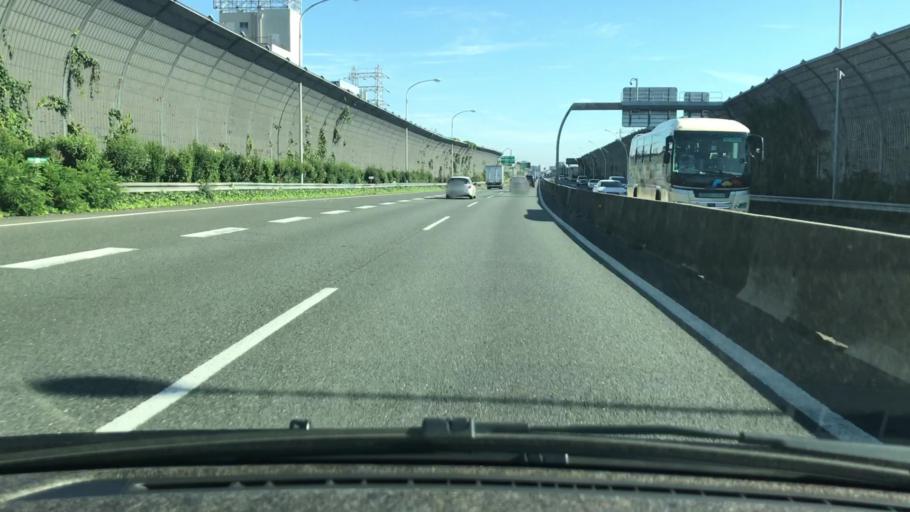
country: JP
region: Osaka
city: Toyonaka
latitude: 34.7552
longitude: 135.4685
